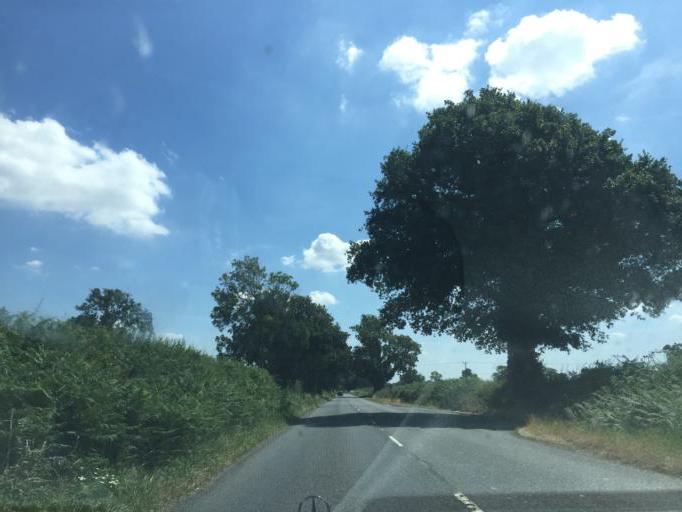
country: GB
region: England
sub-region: Leicestershire
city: Hinckley
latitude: 52.4953
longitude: -1.3562
